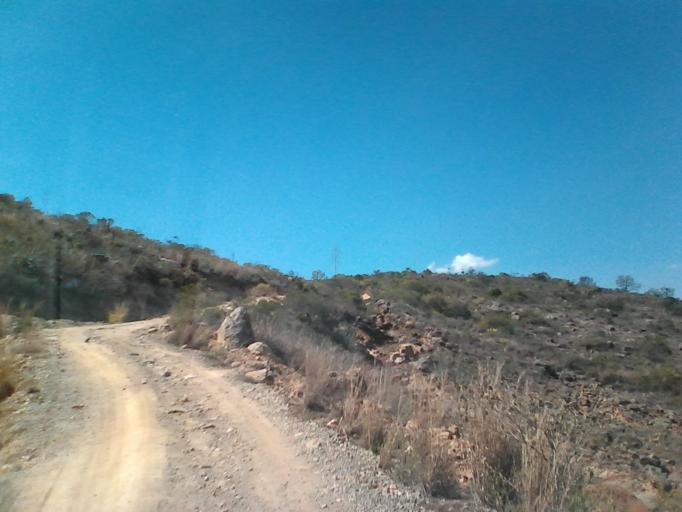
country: CO
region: Boyaca
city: Sachica
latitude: 5.5573
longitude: -73.5643
